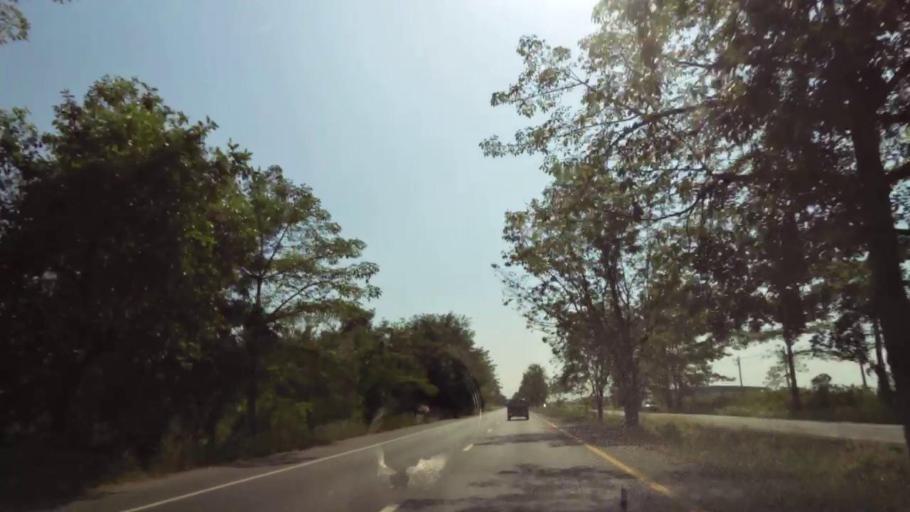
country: TH
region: Nakhon Sawan
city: Kao Liao
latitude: 15.9373
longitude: 100.1132
